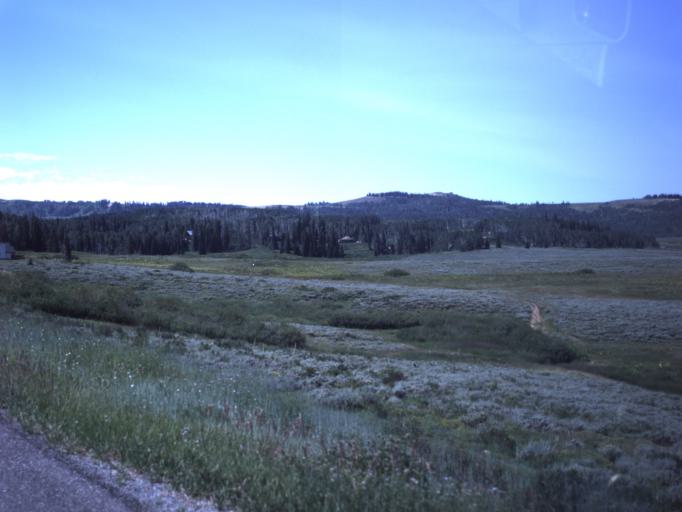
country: US
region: Utah
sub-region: Sanpete County
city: Fairview
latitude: 39.6599
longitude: -111.3012
